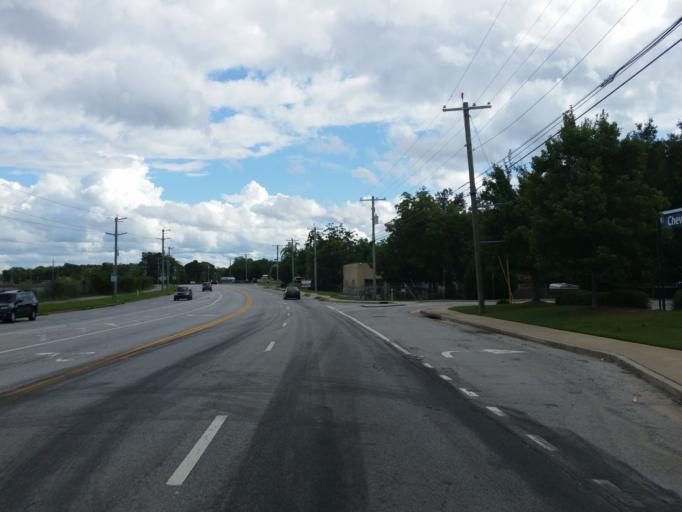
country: US
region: Georgia
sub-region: Cobb County
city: Fair Oaks
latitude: 33.9214
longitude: -84.5427
